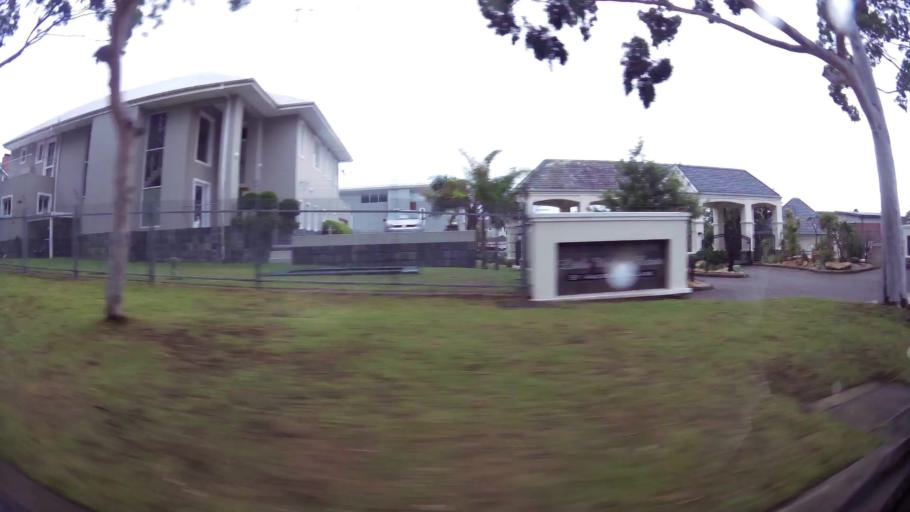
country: ZA
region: Eastern Cape
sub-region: Nelson Mandela Bay Metropolitan Municipality
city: Port Elizabeth
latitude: -33.9741
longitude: 25.5790
